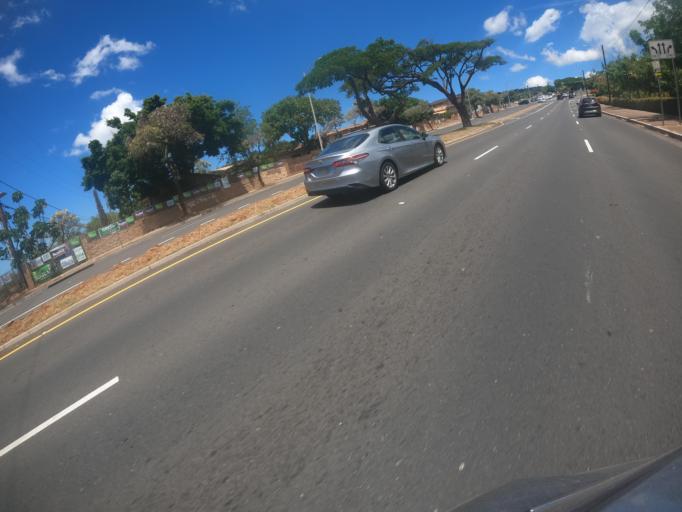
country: US
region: Hawaii
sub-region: Honolulu County
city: Makakilo City
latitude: 21.3436
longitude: -158.0790
